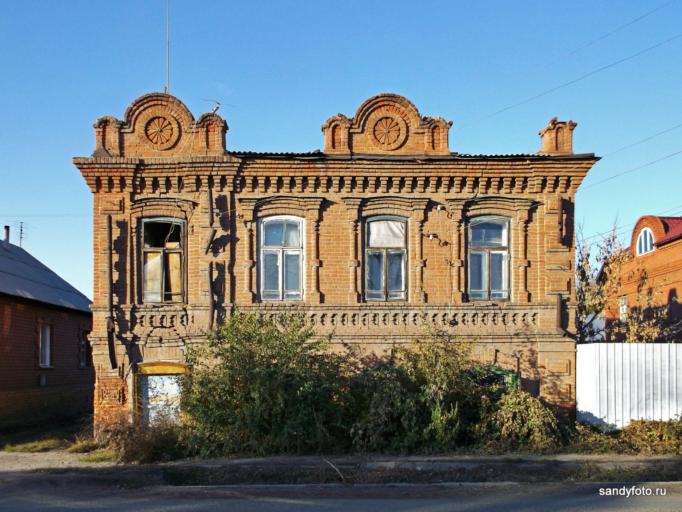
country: RU
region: Chelyabinsk
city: Troitsk
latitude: 54.0967
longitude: 61.5651
